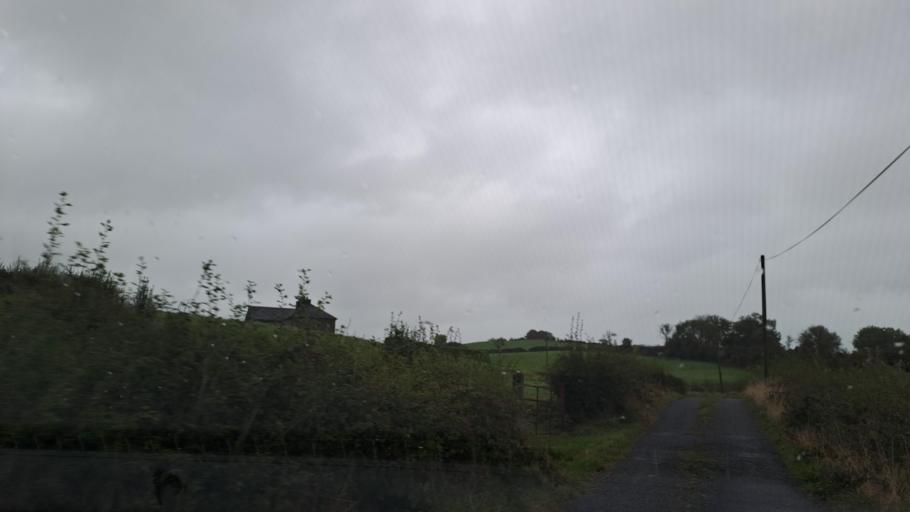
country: IE
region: Ulster
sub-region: An Cabhan
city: Kingscourt
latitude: 54.0066
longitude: -6.8353
